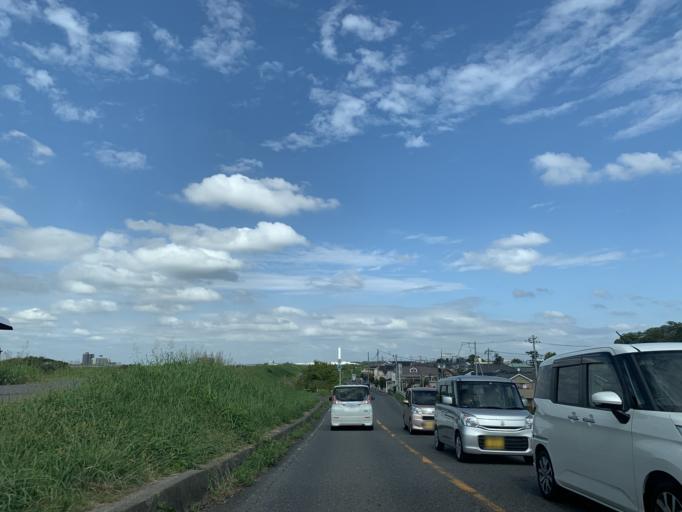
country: JP
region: Chiba
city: Nagareyama
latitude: 35.8462
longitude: 139.8932
